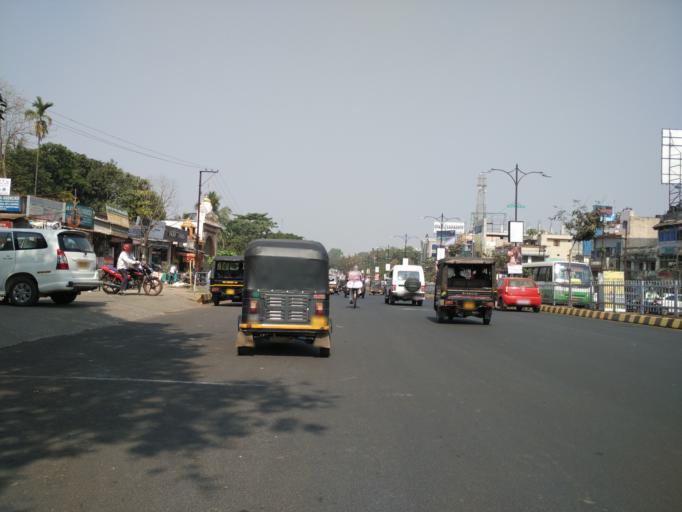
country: IN
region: Odisha
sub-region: Khordha
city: Bhubaneshwar
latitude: 20.2713
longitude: 85.8420
